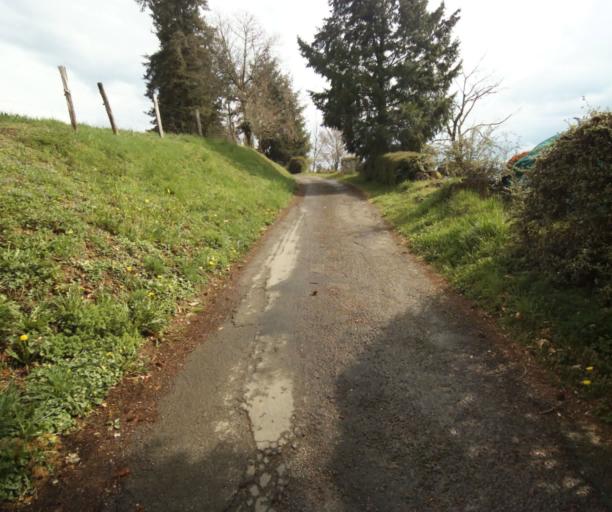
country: FR
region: Limousin
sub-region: Departement de la Correze
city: Tulle
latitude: 45.2847
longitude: 1.7418
